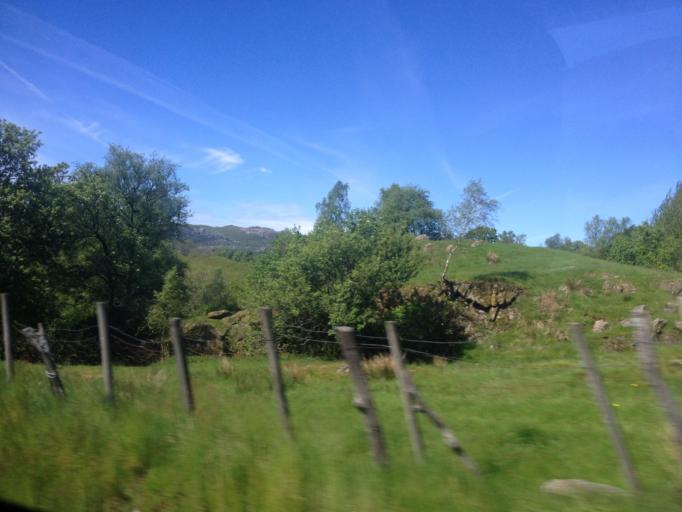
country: NO
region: Rogaland
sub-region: Bjerkreim
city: Vikesa
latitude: 58.5445
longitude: 6.2303
